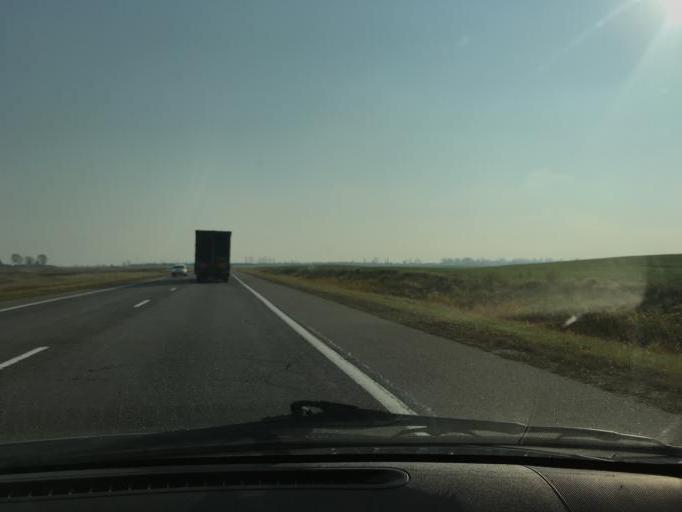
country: BY
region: Vitebsk
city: Chashniki
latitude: 55.0105
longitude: 29.1264
